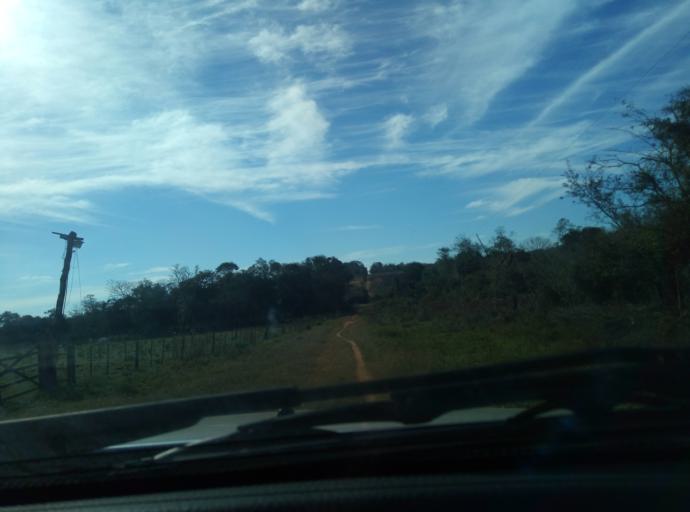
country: PY
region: Caaguazu
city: Carayao
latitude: -25.1677
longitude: -56.2929
